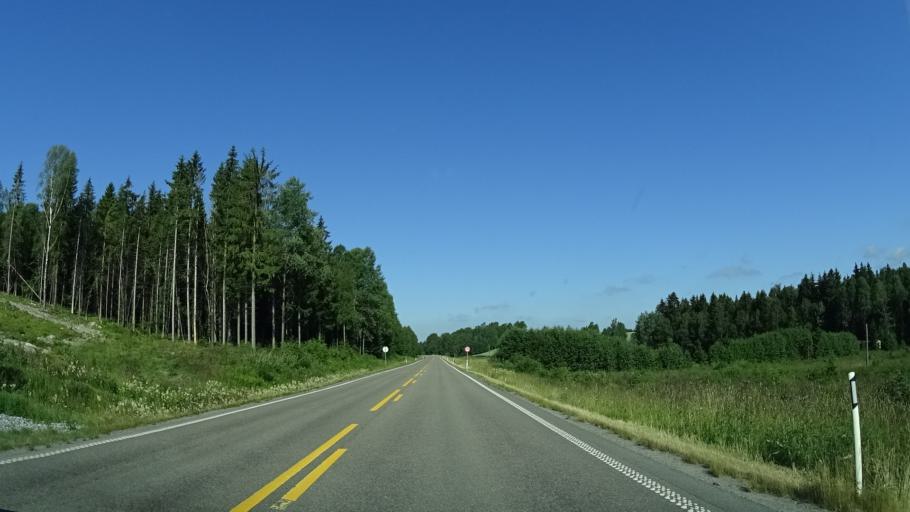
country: NO
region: Akershus
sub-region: Ski
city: Ski
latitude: 59.6817
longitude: 10.8528
